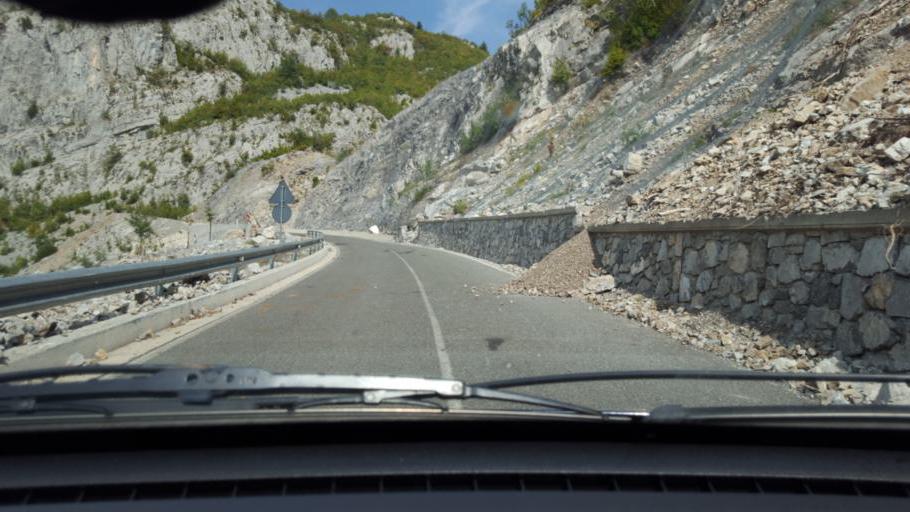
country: AL
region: Shkoder
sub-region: Rrethi i Malesia e Madhe
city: Kastrat
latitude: 42.5225
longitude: 19.6320
